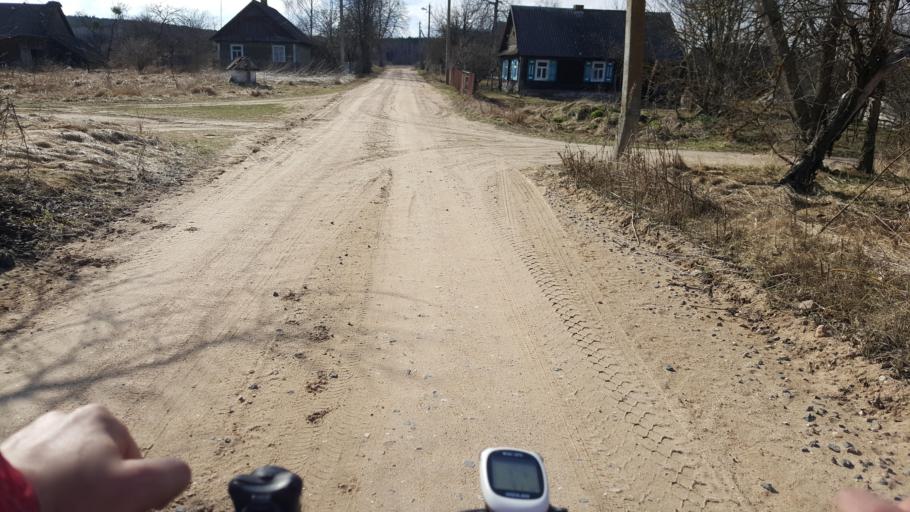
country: BY
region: Brest
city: Kamyanyets
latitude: 52.4016
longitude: 23.9562
